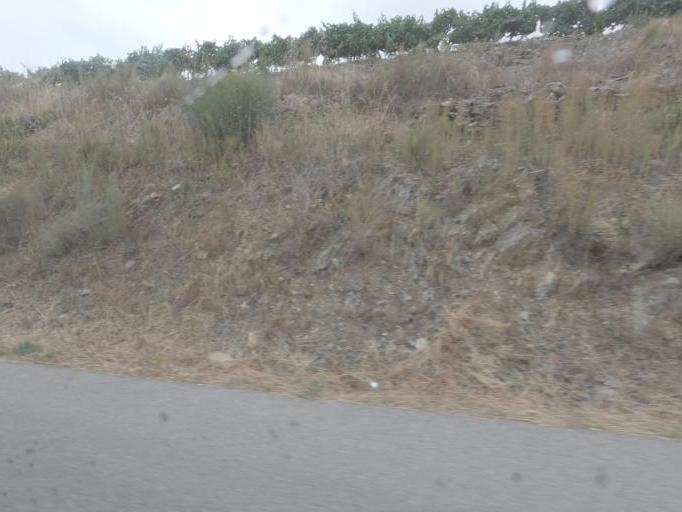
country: PT
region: Vila Real
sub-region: Sabrosa
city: Sabrosa
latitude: 41.2232
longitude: -7.5110
